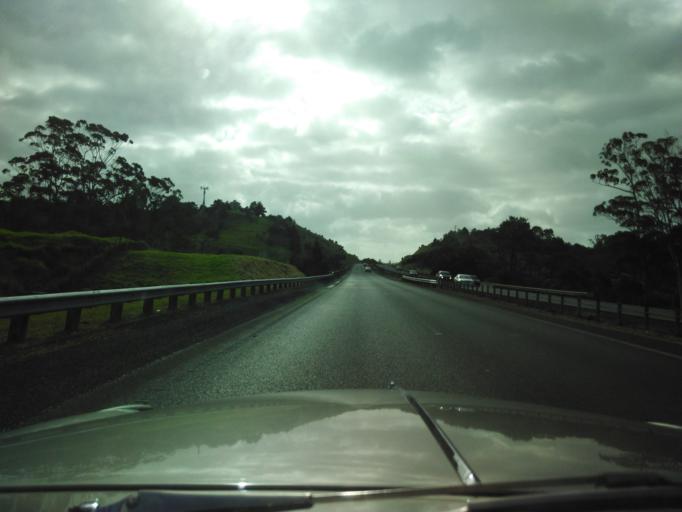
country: NZ
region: Auckland
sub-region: Auckland
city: Rothesay Bay
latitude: -36.5997
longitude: 174.6624
